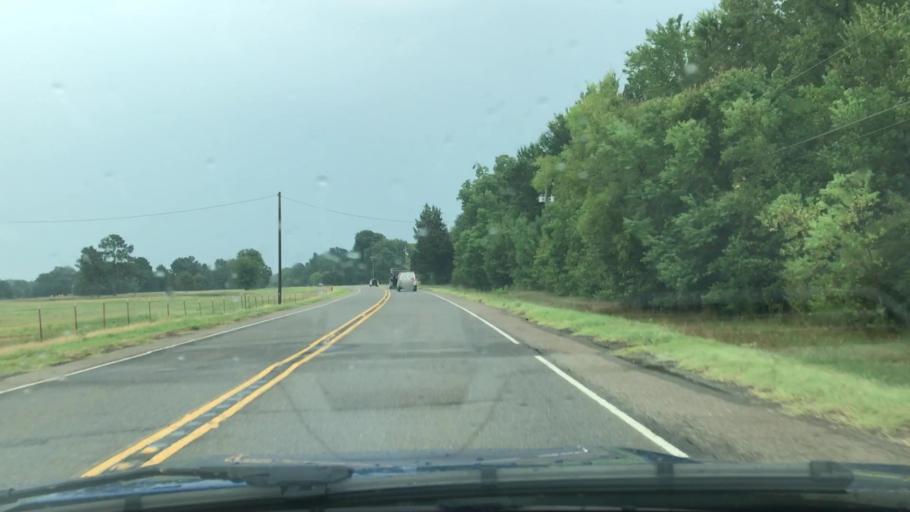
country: US
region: Texas
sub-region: Harrison County
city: Waskom
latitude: 32.4619
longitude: -94.0291
